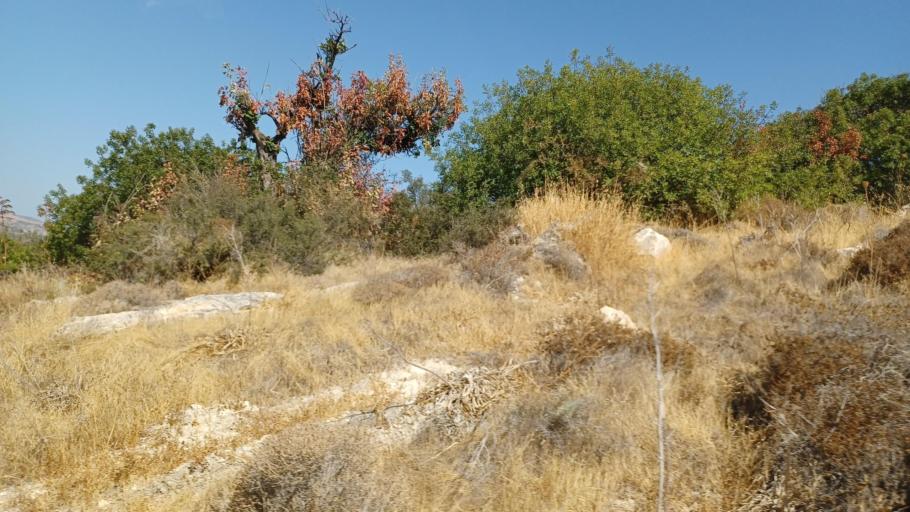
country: CY
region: Pafos
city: Polis
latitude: 34.9708
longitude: 32.4978
